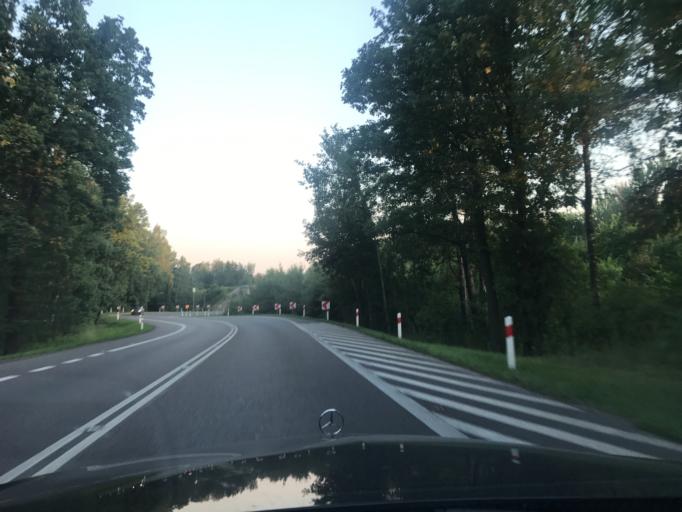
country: PL
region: Lublin Voivodeship
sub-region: Powiat lubelski
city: Niemce
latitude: 51.3881
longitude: 22.6358
